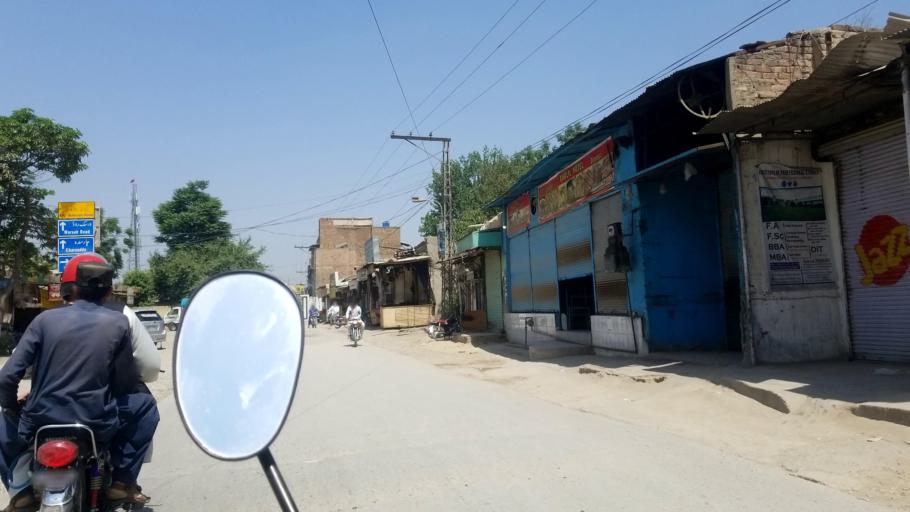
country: PK
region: Khyber Pakhtunkhwa
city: Peshawar
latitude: 34.0219
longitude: 71.4849
